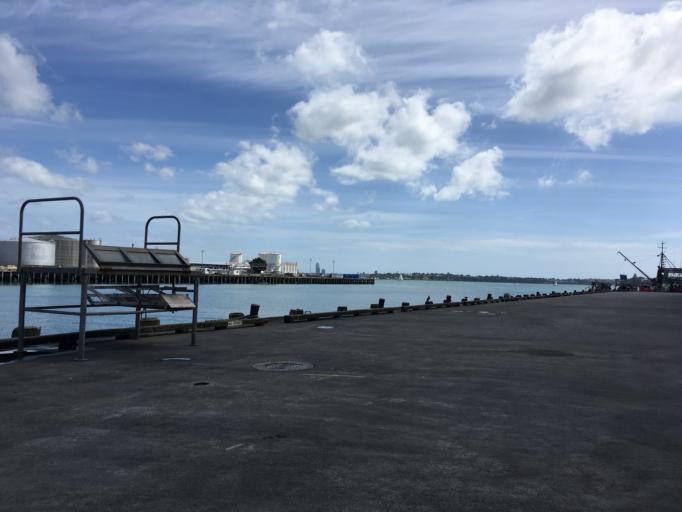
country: NZ
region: Auckland
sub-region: Auckland
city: Auckland
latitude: -36.8408
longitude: 174.7588
